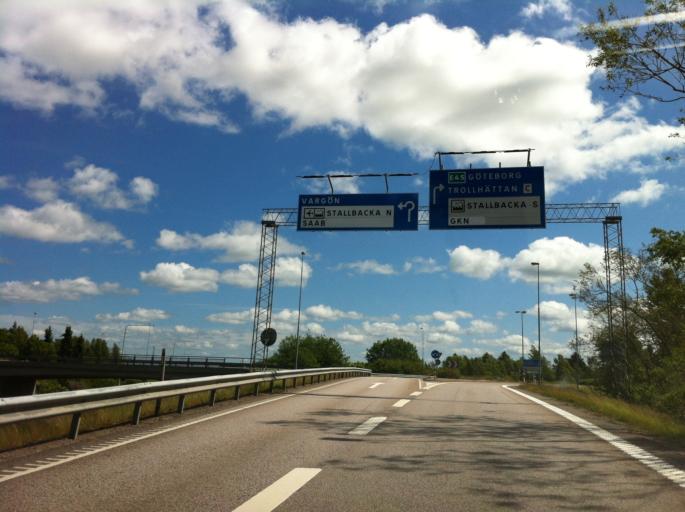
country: SE
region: Vaestra Goetaland
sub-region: Trollhattan
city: Trollhattan
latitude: 58.3023
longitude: 12.3271
